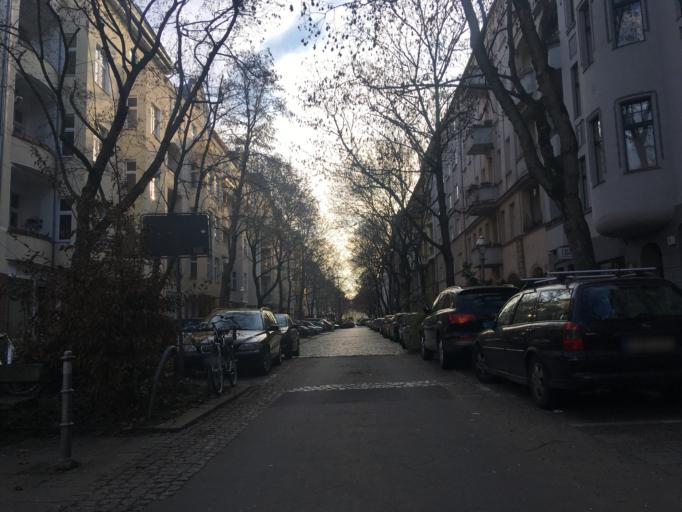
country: DE
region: Berlin
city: Moabit
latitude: 52.5235
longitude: 13.3360
